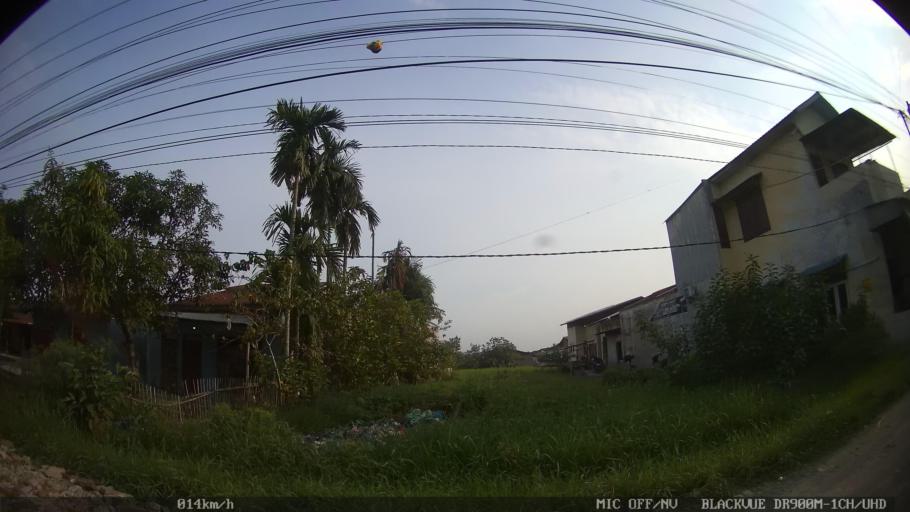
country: ID
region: North Sumatra
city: Medan
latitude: 3.5846
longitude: 98.7552
